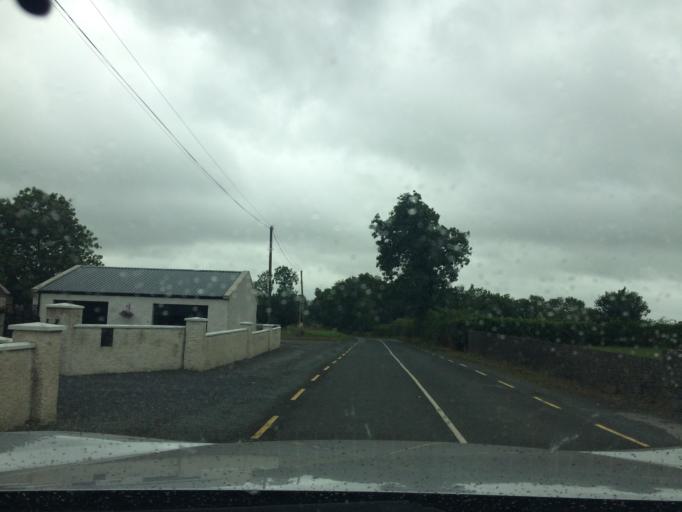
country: IE
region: Munster
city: Cashel
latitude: 52.5505
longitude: -7.8951
